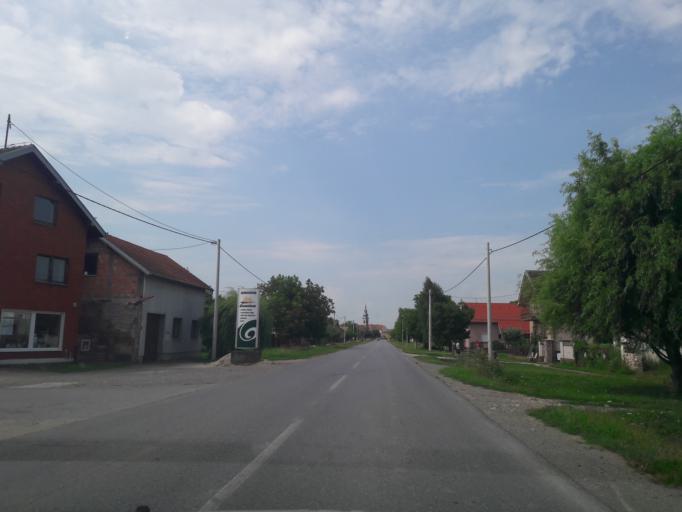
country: HR
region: Osjecko-Baranjska
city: Gorjani
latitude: 45.4636
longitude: 18.3279
